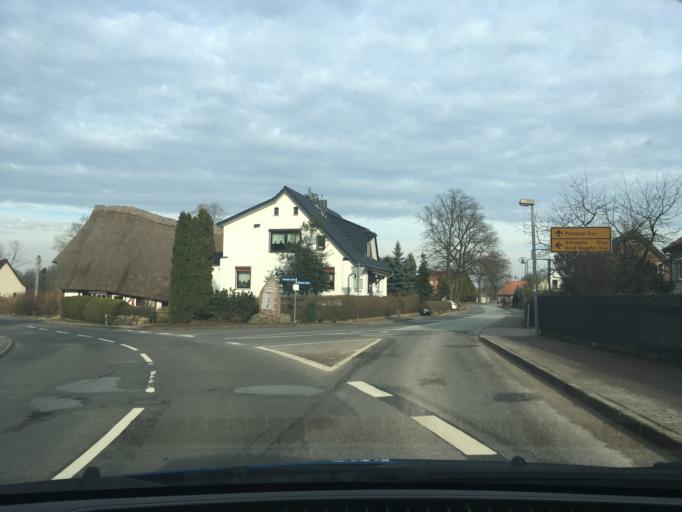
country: DE
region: Mecklenburg-Vorpommern
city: Stralendorf
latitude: 53.5751
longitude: 11.3051
